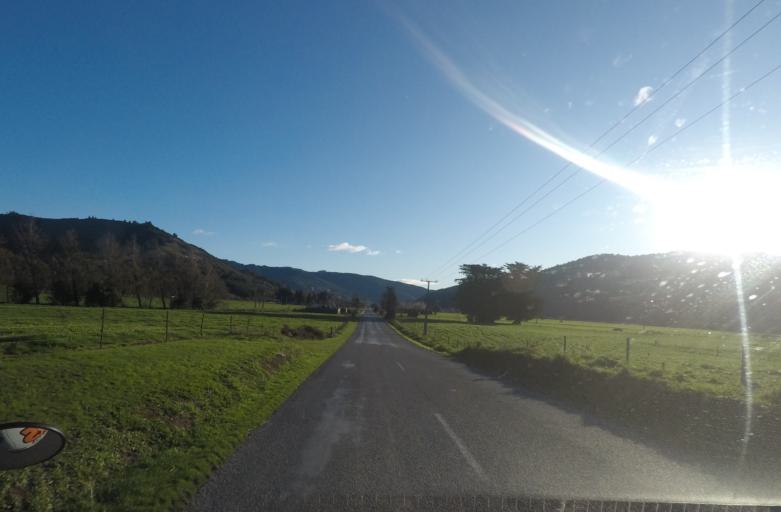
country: NZ
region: Marlborough
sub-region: Marlborough District
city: Picton
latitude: -41.2894
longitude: 173.8641
